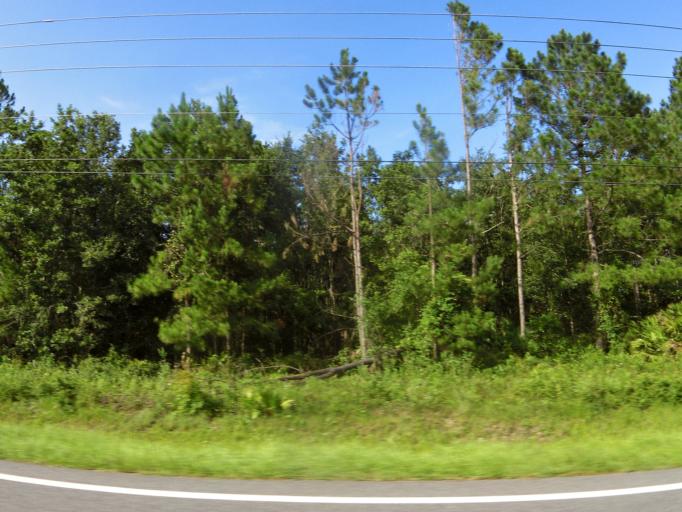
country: US
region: Florida
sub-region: Clay County
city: Green Cove Springs
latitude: 29.9943
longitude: -81.5372
